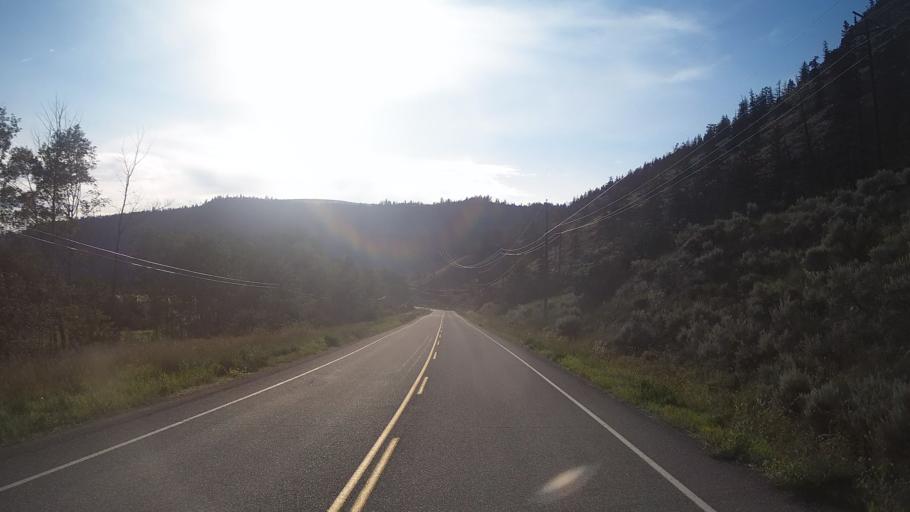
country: CA
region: British Columbia
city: Lillooet
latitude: 50.8973
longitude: -121.7721
